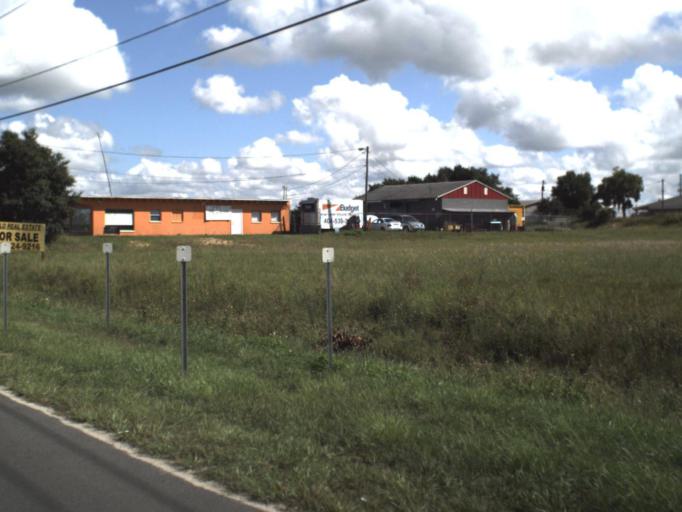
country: US
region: Florida
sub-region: Polk County
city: Haines City
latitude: 28.1146
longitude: -81.6180
